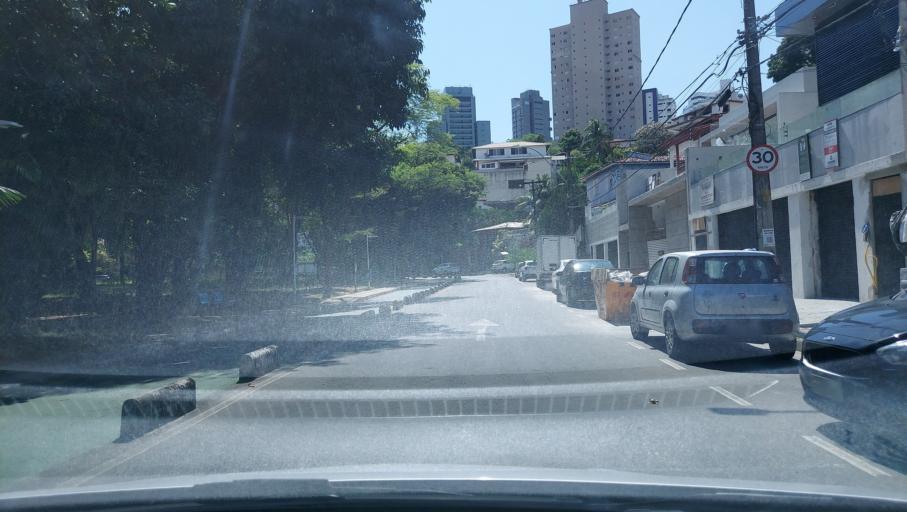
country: BR
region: Bahia
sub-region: Salvador
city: Salvador
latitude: -12.9855
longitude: -38.4564
